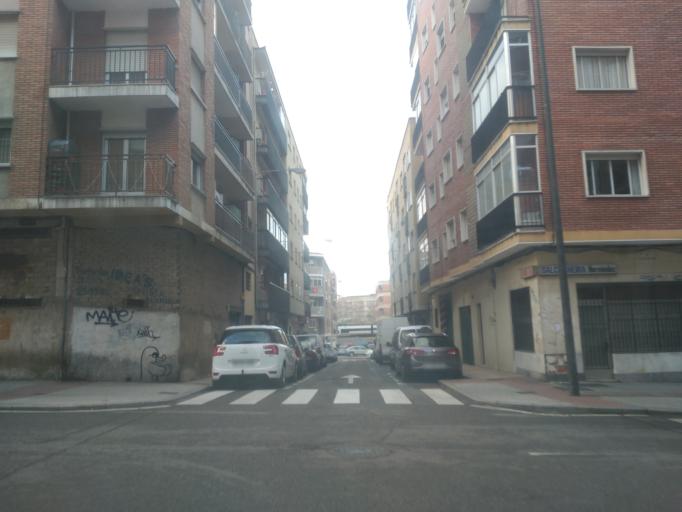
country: ES
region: Castille and Leon
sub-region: Provincia de Salamanca
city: Salamanca
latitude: 40.9663
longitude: -5.6541
